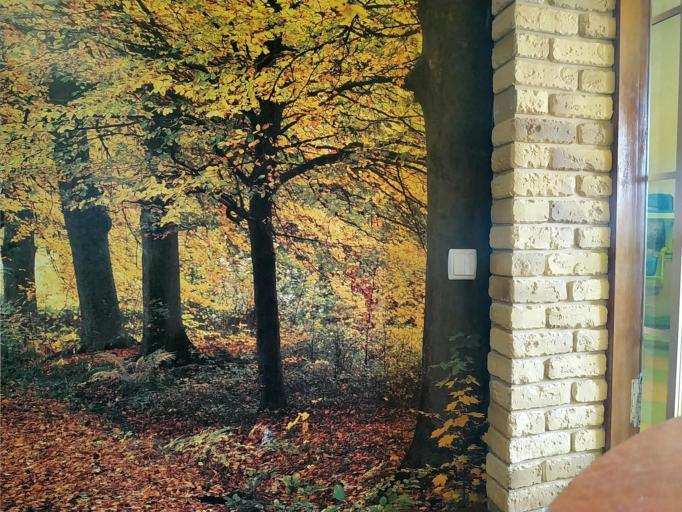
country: RU
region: Smolensk
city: Katyn'
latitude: 54.9311
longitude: 31.7397
